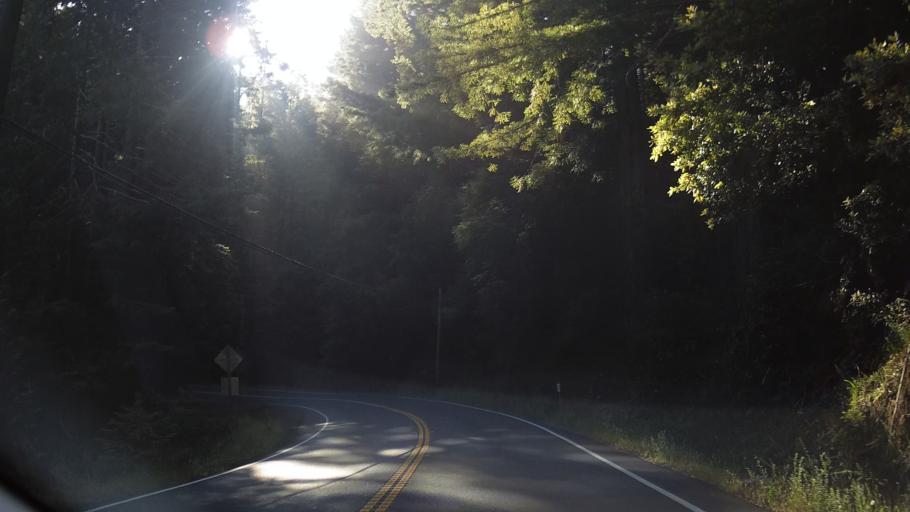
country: US
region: California
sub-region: Mendocino County
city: Fort Bragg
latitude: 39.4065
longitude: -123.7324
